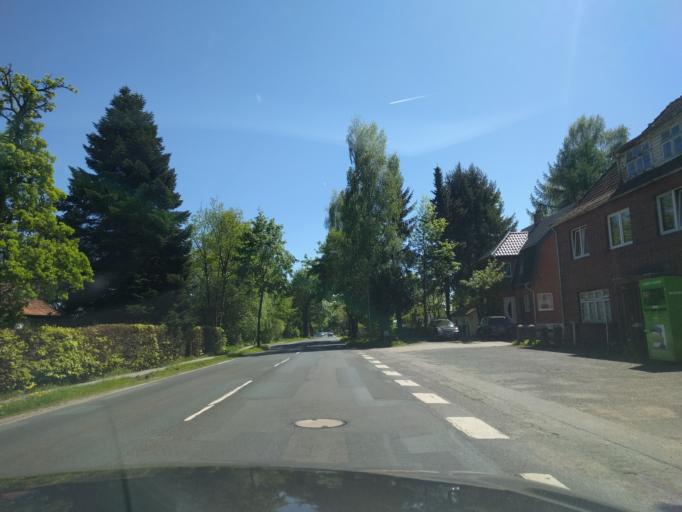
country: DE
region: Lower Saxony
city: Seevetal
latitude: 53.4017
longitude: 10.0049
